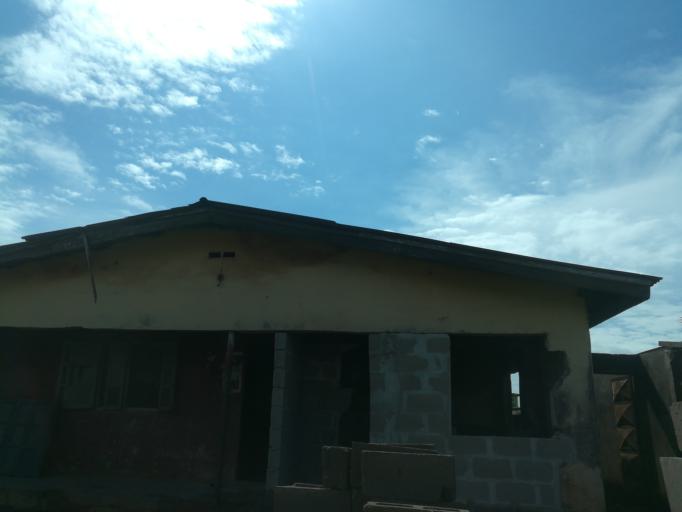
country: NG
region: Lagos
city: Ikorodu
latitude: 6.5943
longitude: 3.5180
